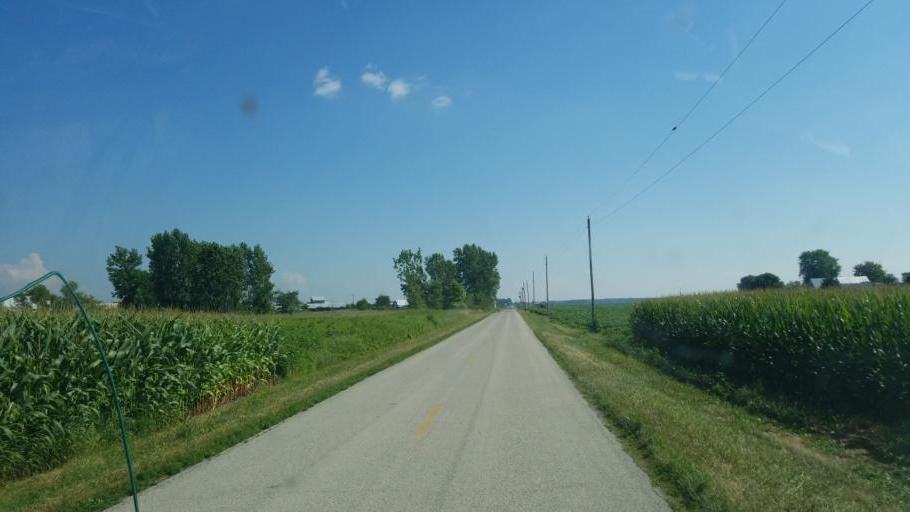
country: US
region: Ohio
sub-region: Hardin County
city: Kenton
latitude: 40.6839
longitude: -83.5144
